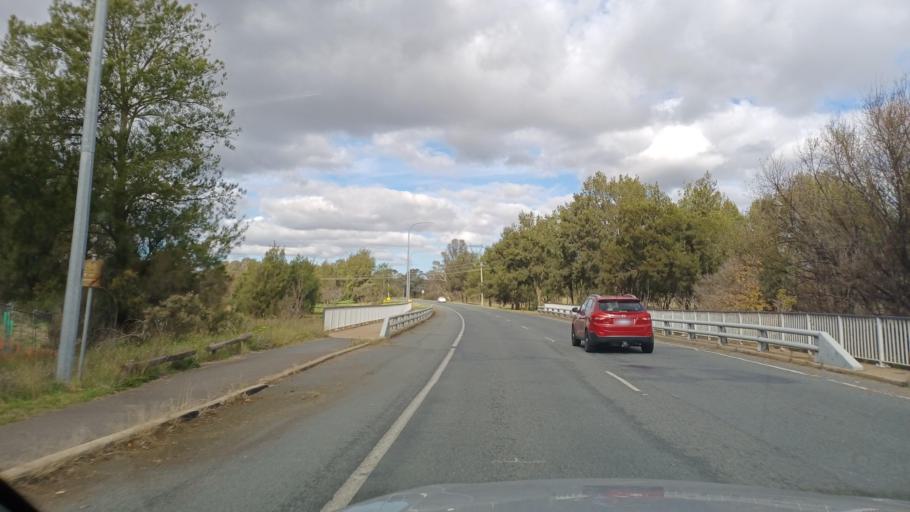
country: AU
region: Australian Capital Territory
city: Belconnen
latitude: -35.2137
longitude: 149.0392
